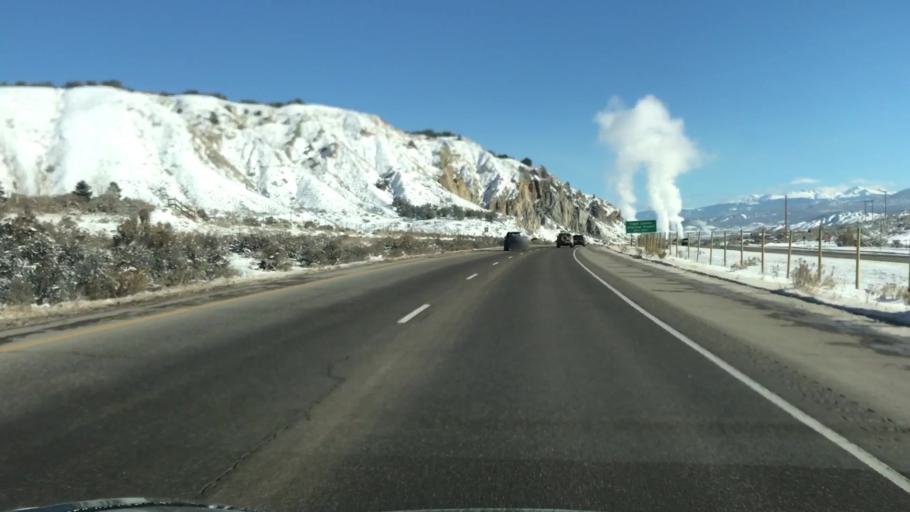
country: US
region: Colorado
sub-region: Eagle County
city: Gypsum
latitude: 39.6558
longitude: -106.9716
